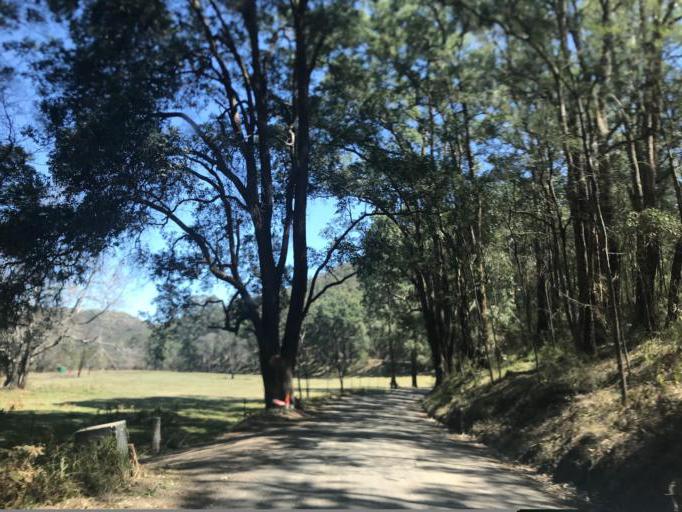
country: AU
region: New South Wales
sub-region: Wyong Shire
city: Little Jilliby
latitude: -33.1989
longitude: 151.0012
